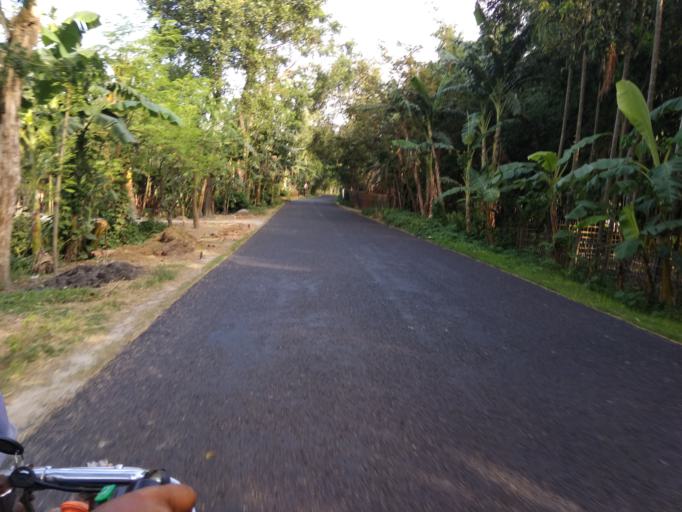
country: BD
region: Rangpur Division
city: Rangpur
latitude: 25.8360
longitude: 89.1151
